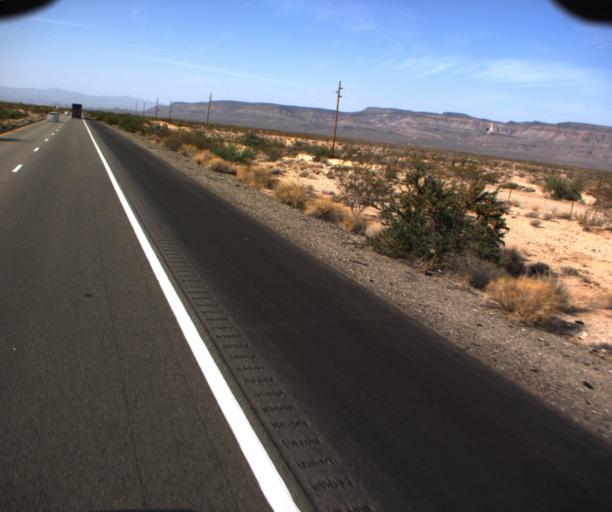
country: US
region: Arizona
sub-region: Mohave County
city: Kingman
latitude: 34.9457
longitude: -114.1471
